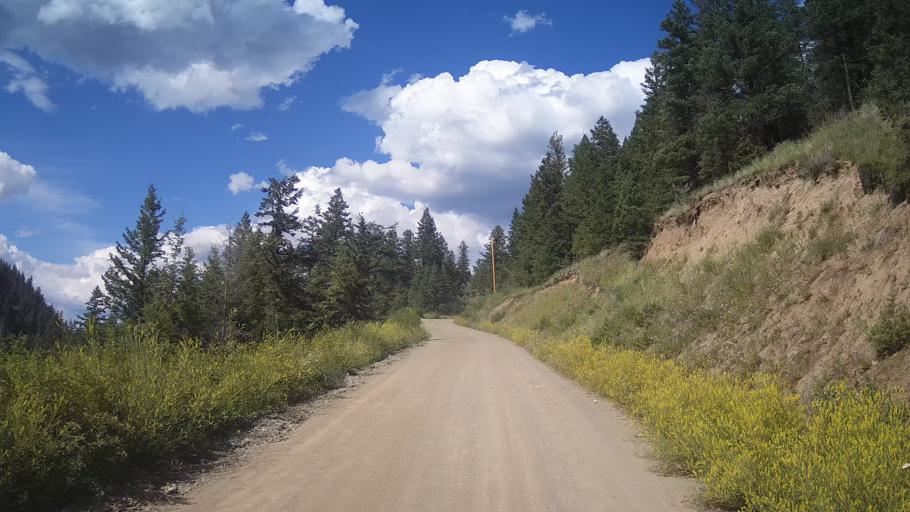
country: CA
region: British Columbia
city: Lillooet
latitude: 51.2602
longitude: -121.9864
